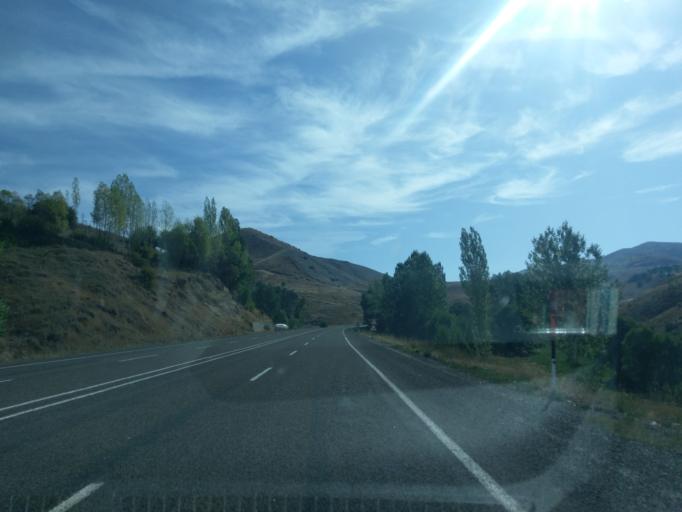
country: TR
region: Sivas
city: Akincilar
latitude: 39.8617
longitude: 38.3481
